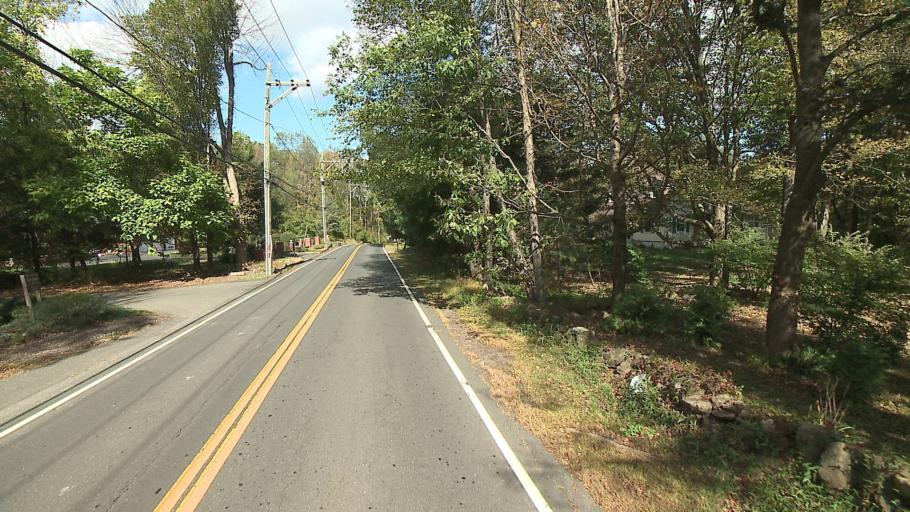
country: US
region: Connecticut
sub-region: New Haven County
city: Cheshire
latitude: 41.4752
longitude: -72.9310
